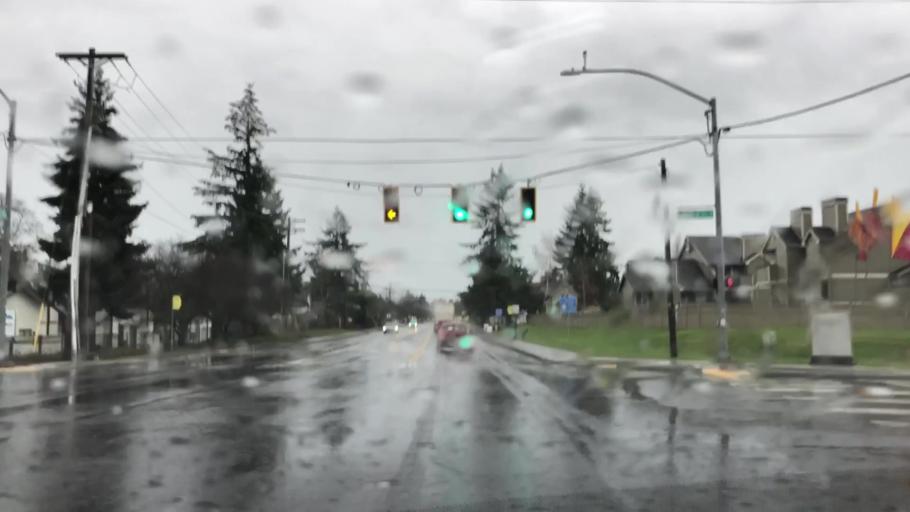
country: US
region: Washington
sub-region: Pierce County
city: McChord Air Force Base
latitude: 47.1595
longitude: -122.4950
